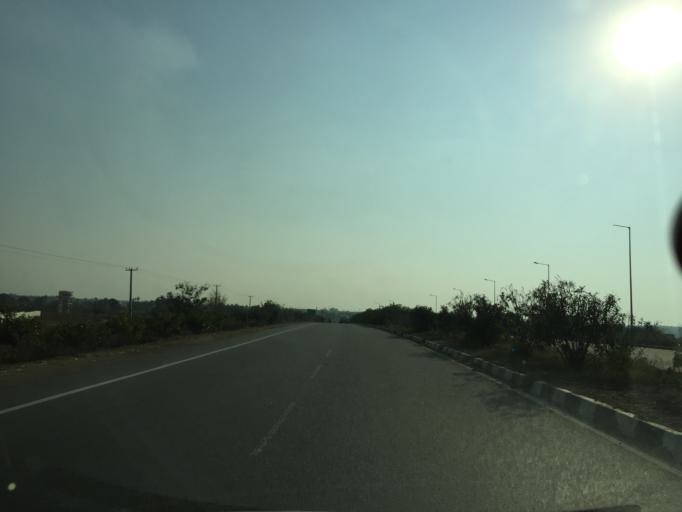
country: IN
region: Telangana
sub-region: Nalgonda
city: Bhongir
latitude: 17.5096
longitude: 78.8989
